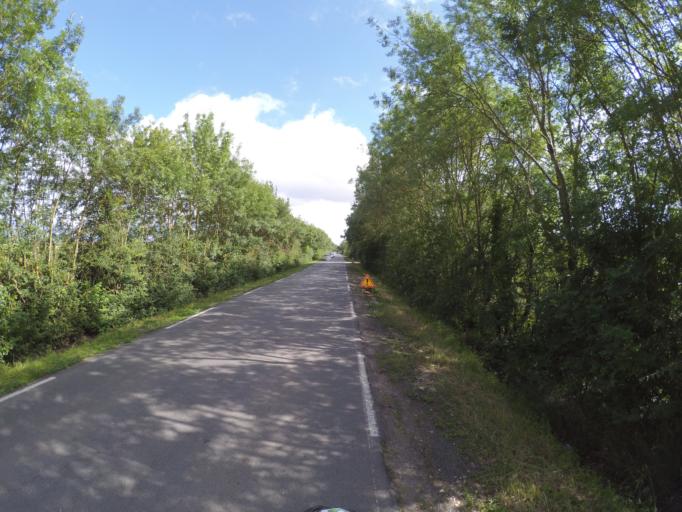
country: FR
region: Aquitaine
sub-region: Departement de la Gironde
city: Saint-Louis-de-Montferrand
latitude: 44.9618
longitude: -0.5519
